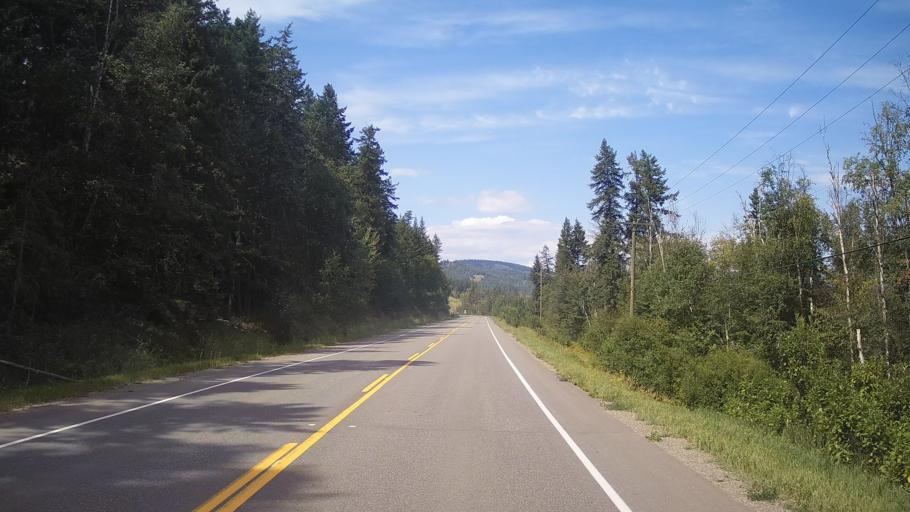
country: CA
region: British Columbia
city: Kamloops
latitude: 51.2466
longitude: -120.1717
